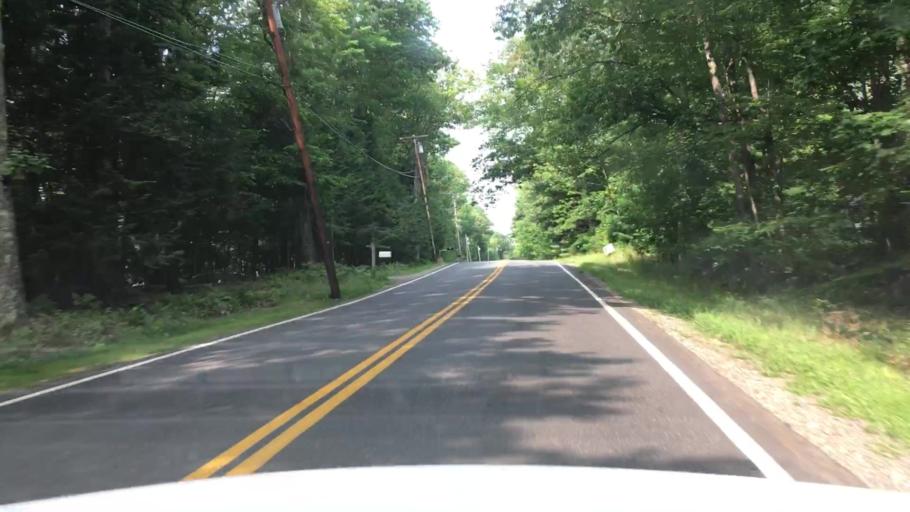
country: US
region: Maine
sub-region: Kennebec County
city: Chelsea
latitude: 44.3130
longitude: -69.6954
